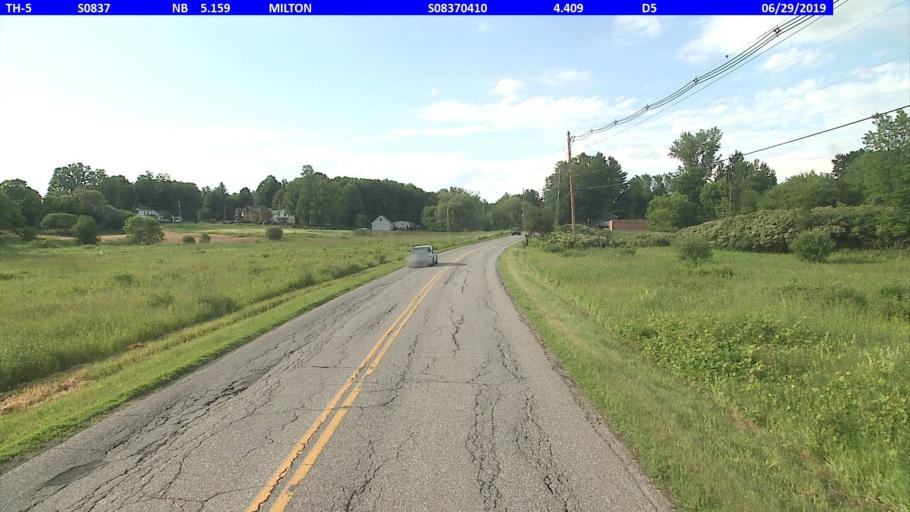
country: US
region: Vermont
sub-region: Chittenden County
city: Milton
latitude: 44.6362
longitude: -73.1015
